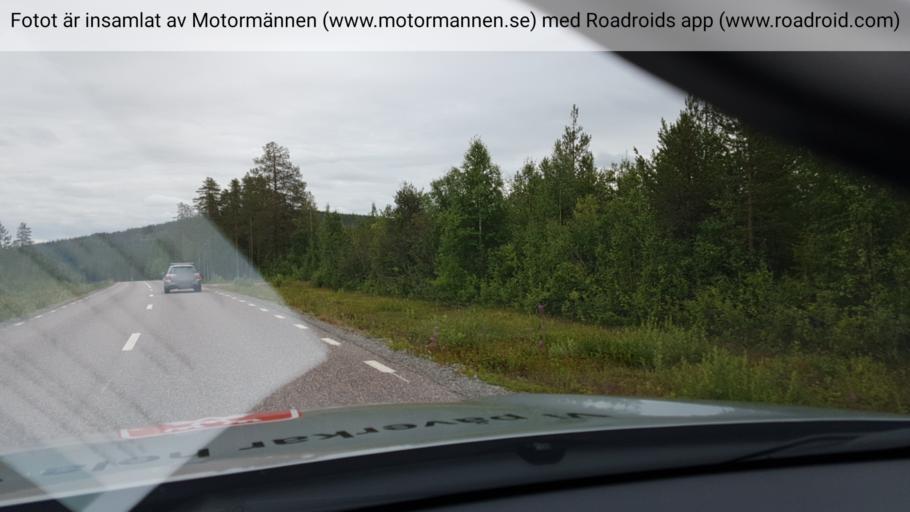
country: SE
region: Norrbotten
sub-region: Gallivare Kommun
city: Gaellivare
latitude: 67.0314
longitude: 21.7171
